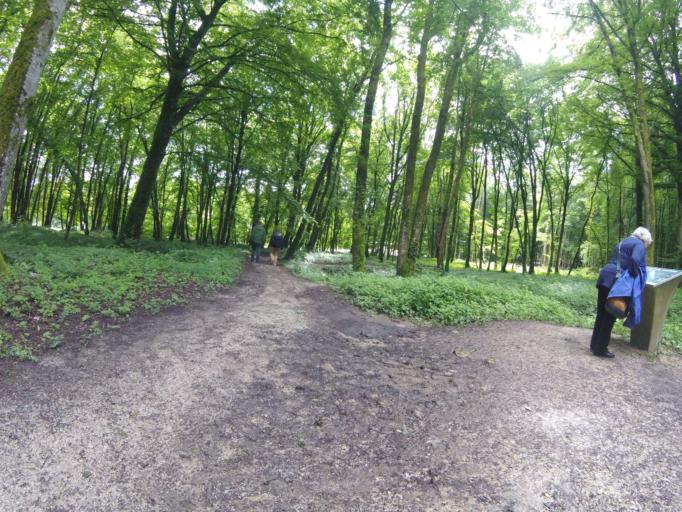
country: FR
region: Lorraine
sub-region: Departement de la Meuse
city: Belleville-sur-Meuse
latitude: 49.2729
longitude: 5.4044
